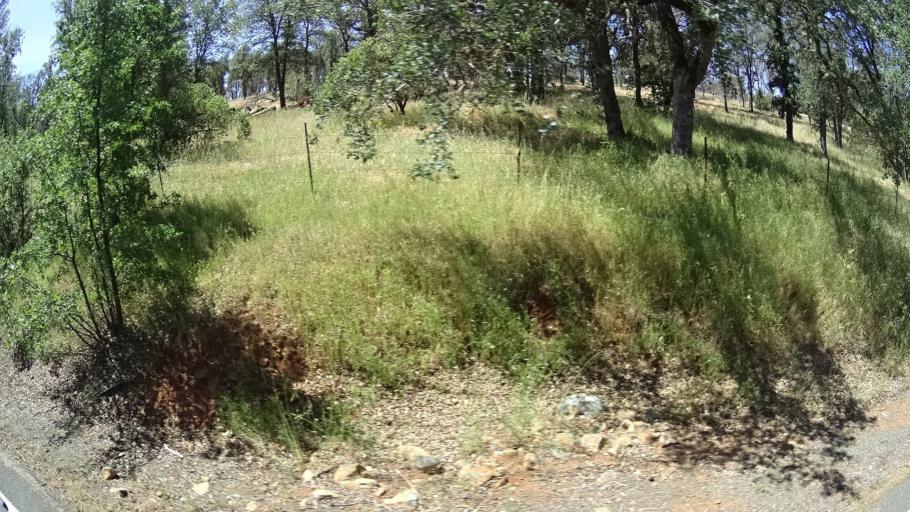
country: US
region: California
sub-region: Lake County
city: Middletown
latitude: 38.7471
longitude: -122.5856
